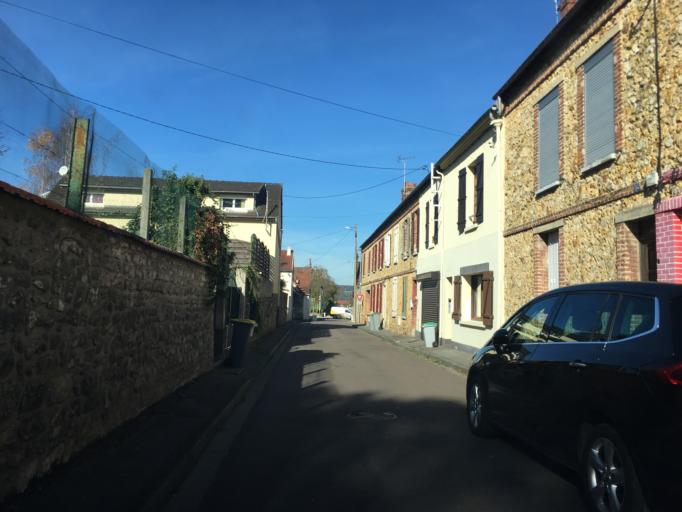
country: FR
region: Haute-Normandie
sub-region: Departement de l'Eure
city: Vernon
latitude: 49.0908
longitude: 1.4574
